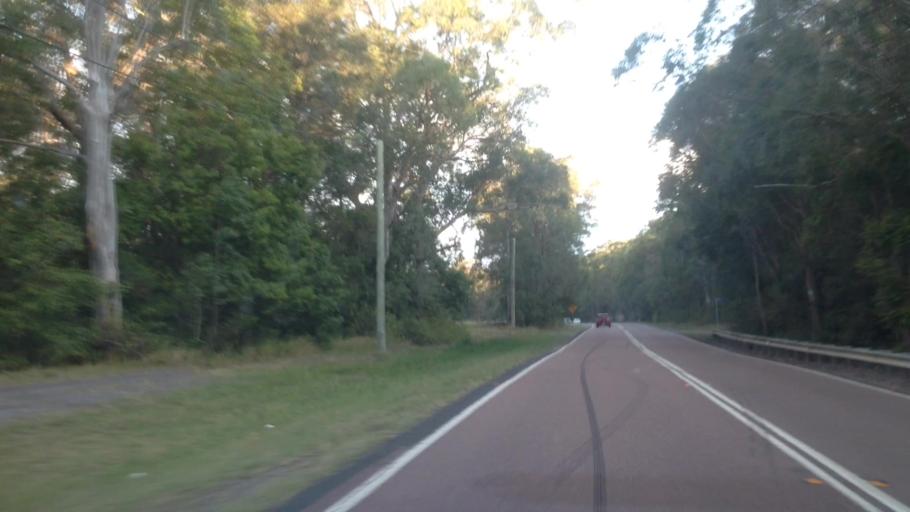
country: AU
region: New South Wales
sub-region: Lake Macquarie Shire
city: Dora Creek
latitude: -32.9908
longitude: 151.4892
